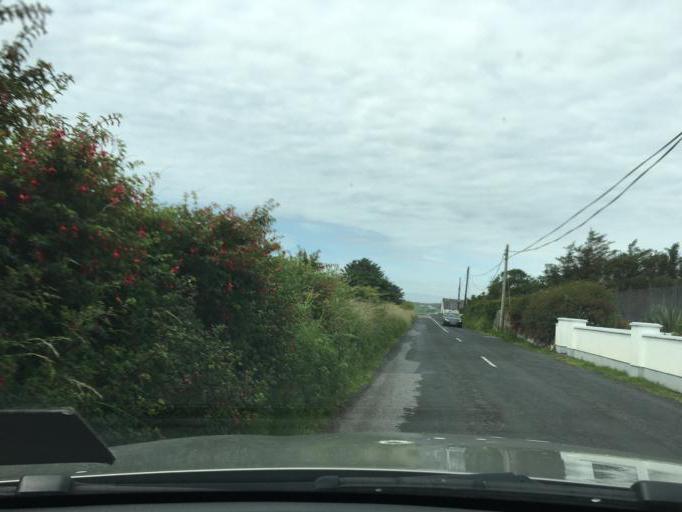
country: IE
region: Ulster
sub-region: County Donegal
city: Carndonagh
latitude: 55.3540
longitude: -7.3237
